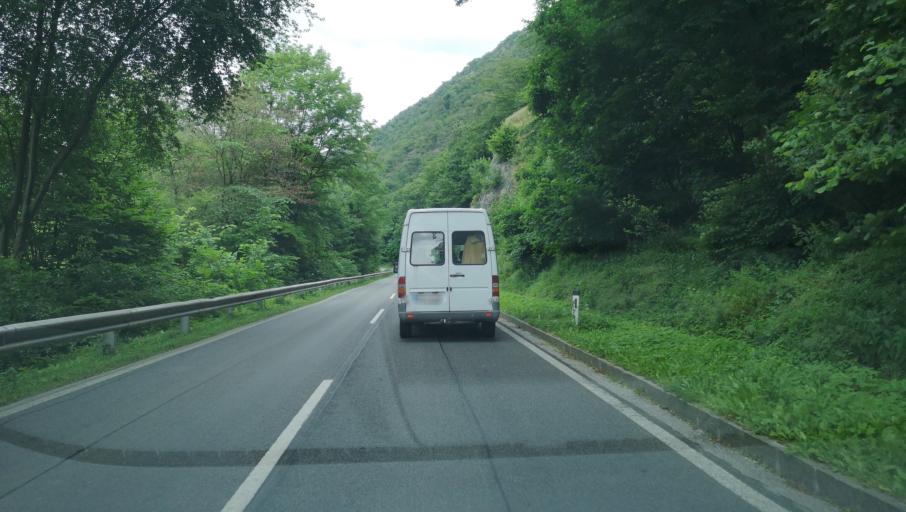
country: AT
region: Lower Austria
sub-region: Politischer Bezirk Krems
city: Aggsbach
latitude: 48.2777
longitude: 15.3986
